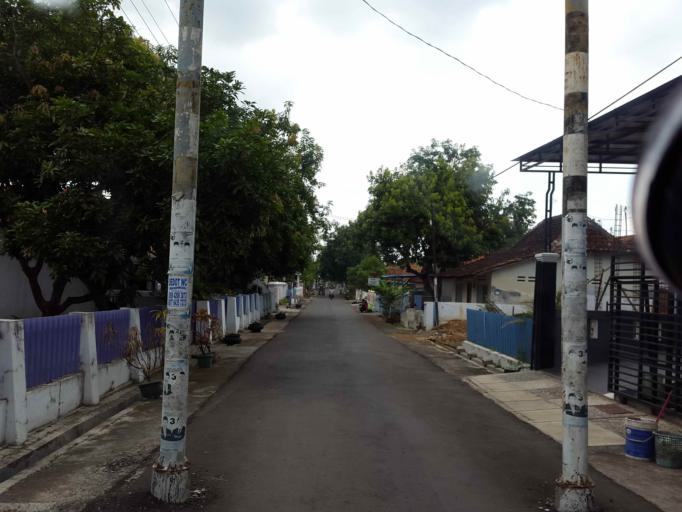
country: ID
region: Central Java
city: Pemalang
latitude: -6.9332
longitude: 109.3883
